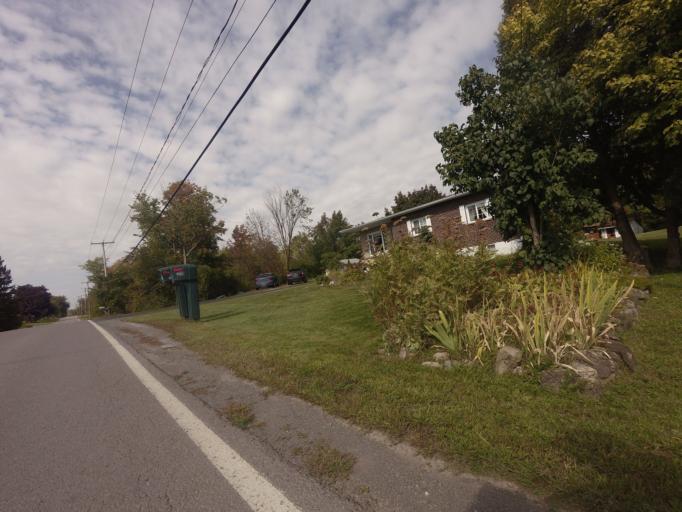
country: CA
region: Quebec
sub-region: Laurentides
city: Blainville
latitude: 45.6189
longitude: -73.9064
